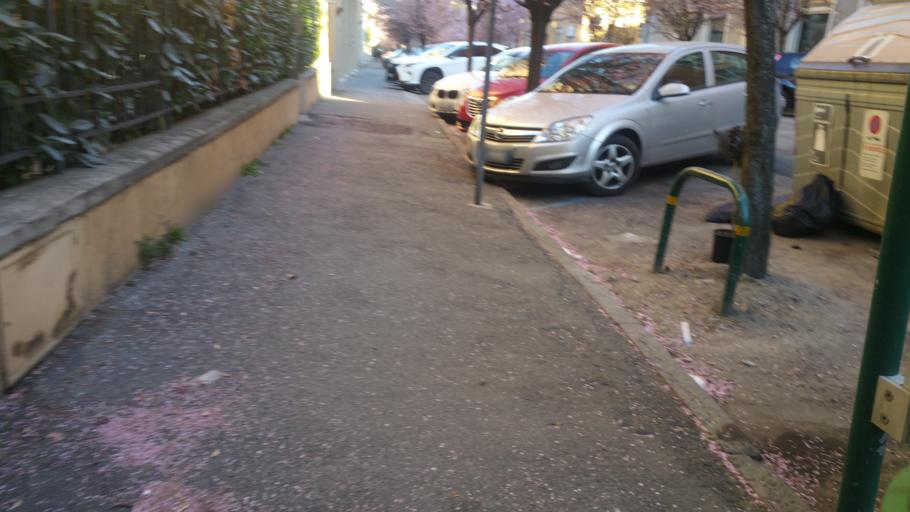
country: IT
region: Emilia-Romagna
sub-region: Provincia di Bologna
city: Bologna
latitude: 44.5011
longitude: 11.3251
